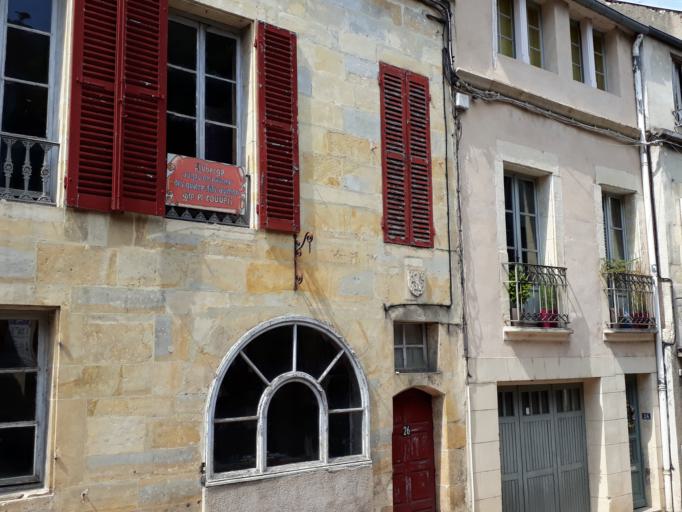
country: FR
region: Bourgogne
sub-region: Departement de la Nievre
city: Nevers
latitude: 46.9879
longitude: 3.1610
